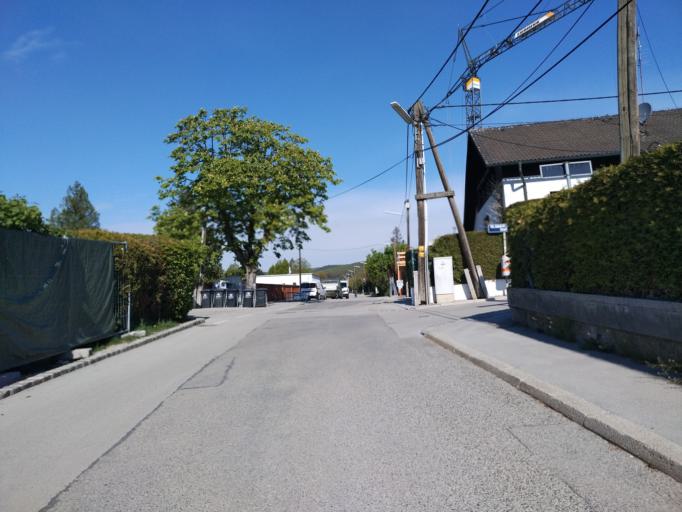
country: AT
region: Lower Austria
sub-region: Politischer Bezirk Wien-Umgebung
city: Purkersdorf
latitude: 48.2078
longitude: 16.2355
